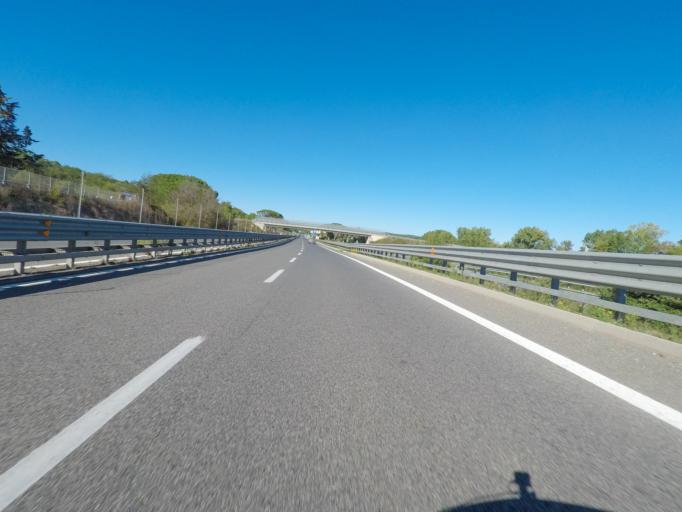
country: IT
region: Tuscany
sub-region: Provincia di Grosseto
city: Campagnatico
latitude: 42.9252
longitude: 11.2645
